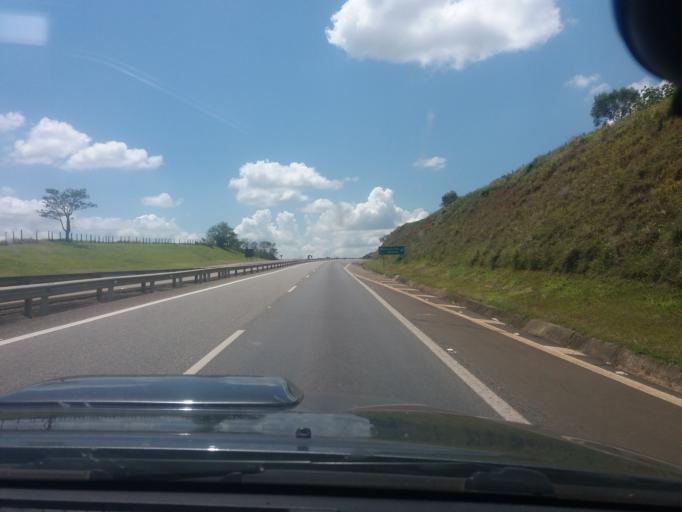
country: BR
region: Sao Paulo
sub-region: Itapetininga
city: Itapetininga
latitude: -23.4895
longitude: -47.9702
